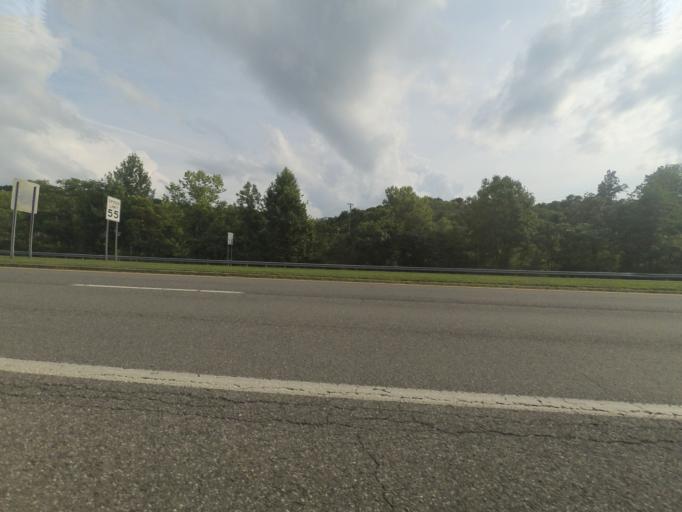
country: US
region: West Virginia
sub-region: Cabell County
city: Huntington
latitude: 38.3971
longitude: -82.4188
